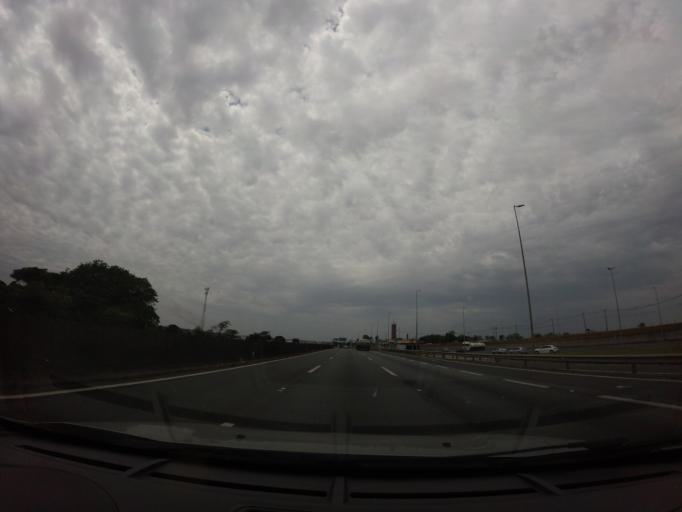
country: BR
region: Sao Paulo
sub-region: Hortolandia
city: Hortolandia
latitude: -22.8121
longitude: -47.2113
